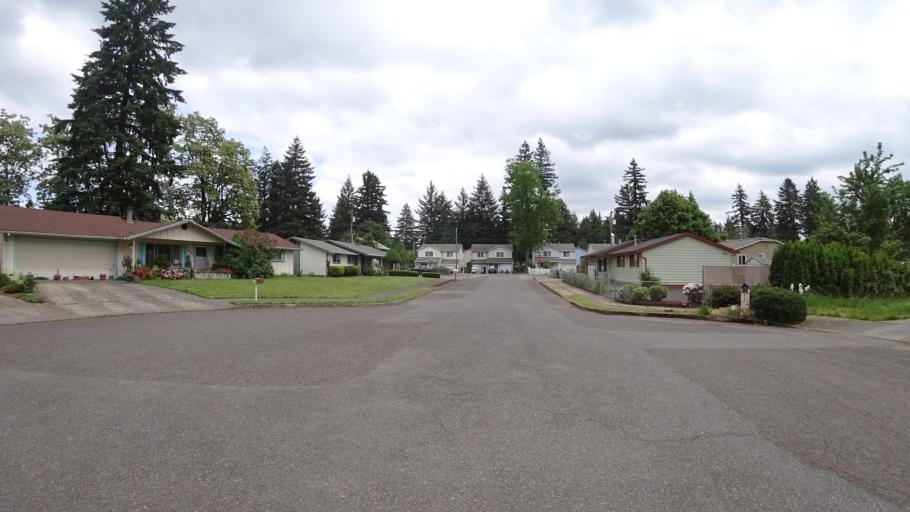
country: US
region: Oregon
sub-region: Multnomah County
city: Lents
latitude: 45.5067
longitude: -122.5488
